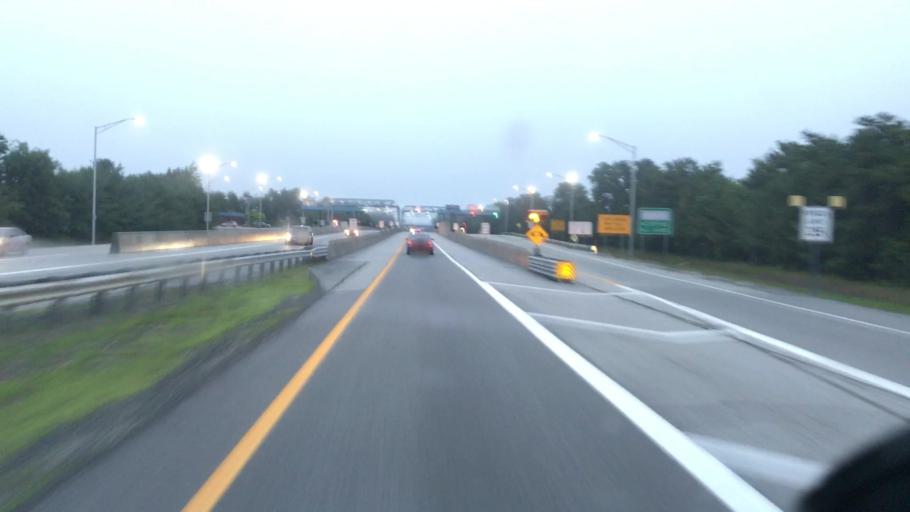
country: US
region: Maine
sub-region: Cumberland County
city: New Gloucester
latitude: 43.9337
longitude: -70.3353
